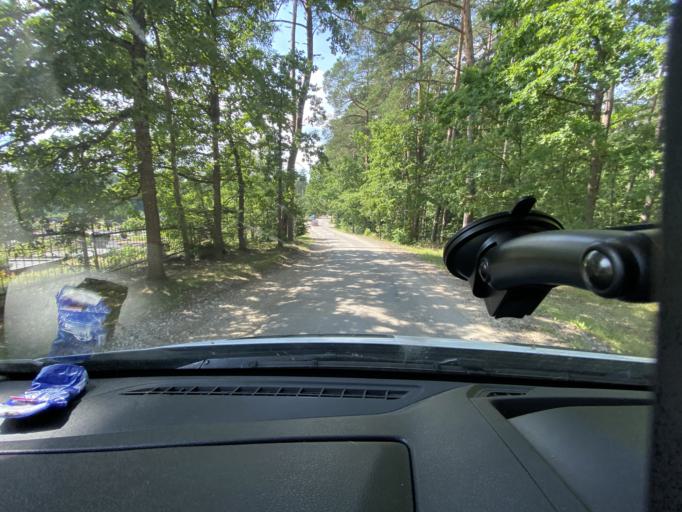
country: LT
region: Kauno apskritis
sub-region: Kauno rajonas
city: Karmelava
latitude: 54.9753
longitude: 24.0421
